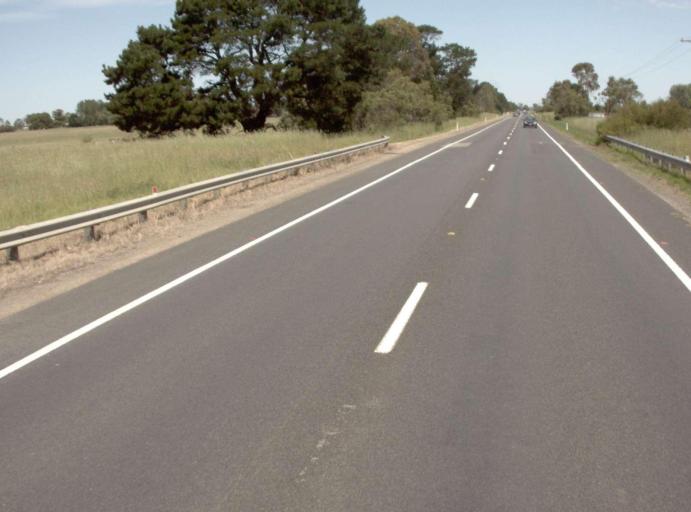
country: AU
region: Victoria
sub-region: Wellington
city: Sale
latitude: -38.0481
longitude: 147.0649
